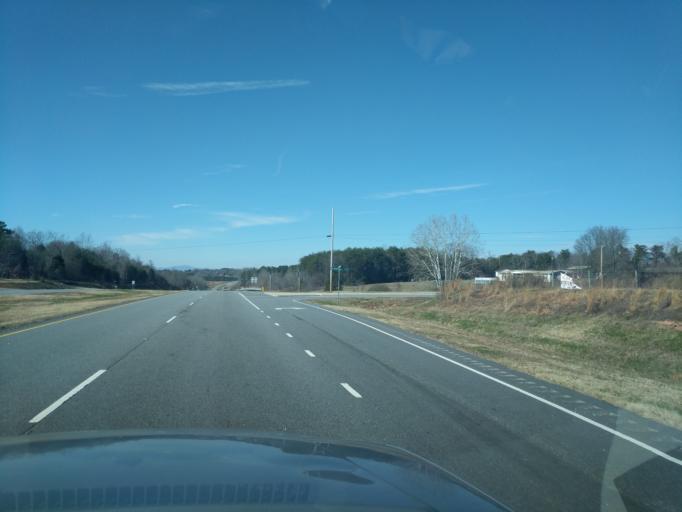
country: US
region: North Carolina
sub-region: Rutherford County
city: Forest City
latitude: 35.2404
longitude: -81.8556
